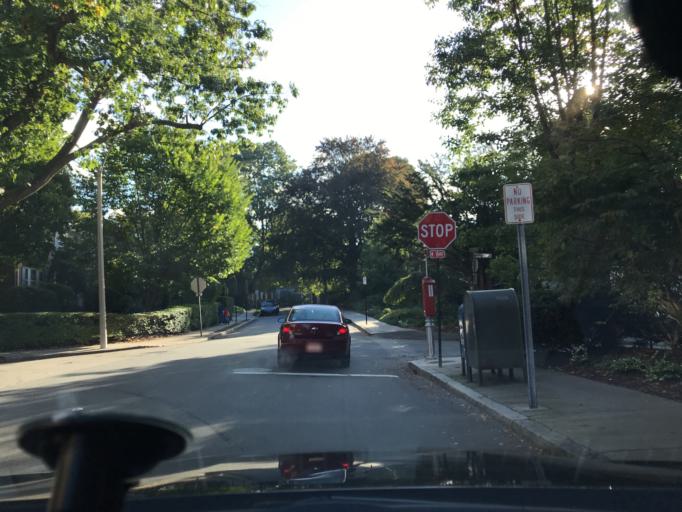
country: US
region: Massachusetts
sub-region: Norfolk County
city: Brookline
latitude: 42.3419
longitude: -71.1148
